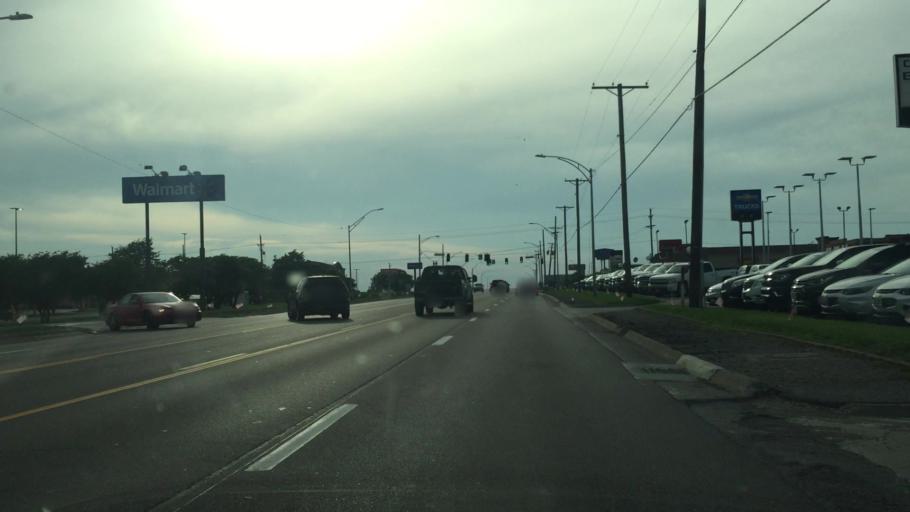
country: US
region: Missouri
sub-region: Pettis County
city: Sedalia
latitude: 38.7097
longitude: -93.2683
